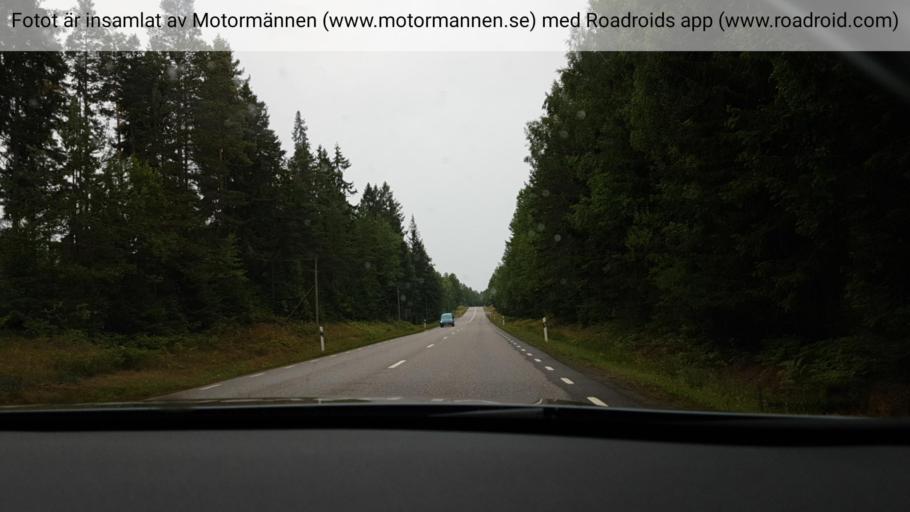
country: SE
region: Joenkoeping
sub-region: Varnamo Kommun
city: Bor
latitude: 57.2360
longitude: 14.1595
